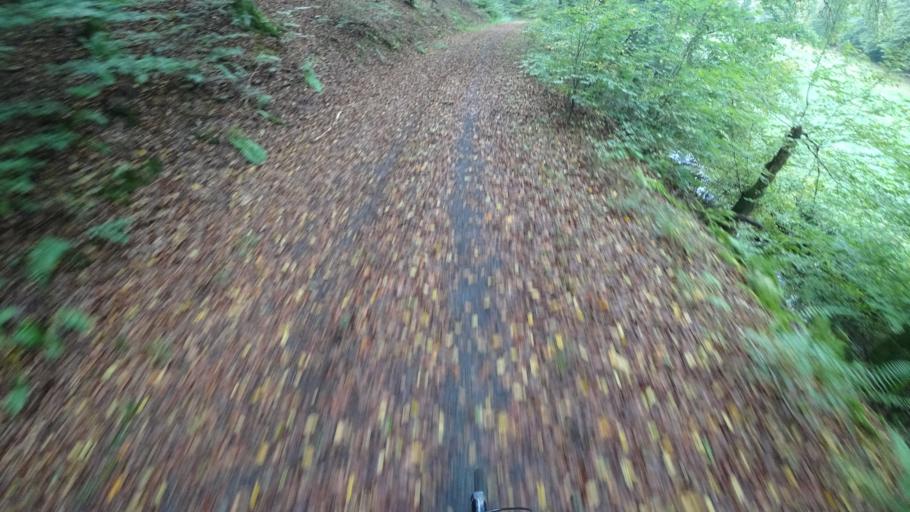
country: DE
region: Rheinland-Pfalz
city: Isselbach
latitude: 50.4038
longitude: 7.9043
